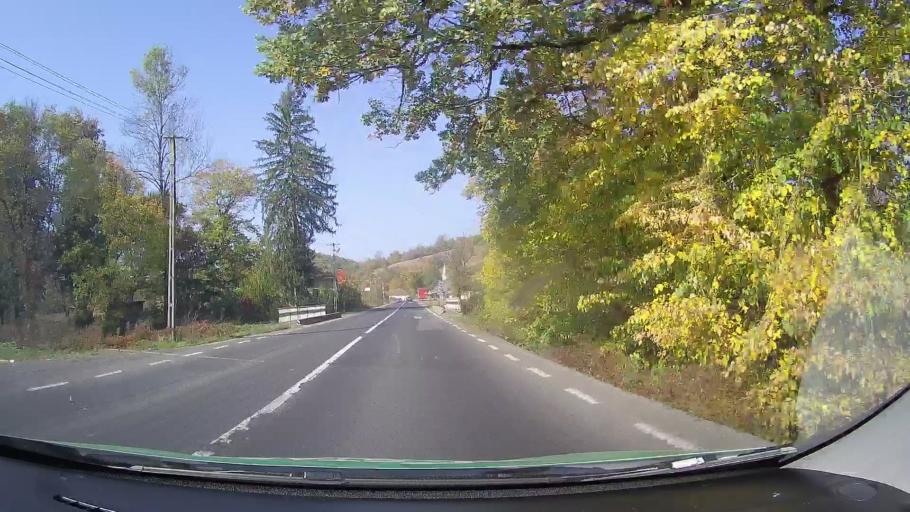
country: RO
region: Arad
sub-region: Comuna Petris
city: Petris
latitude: 46.0146
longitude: 22.3620
